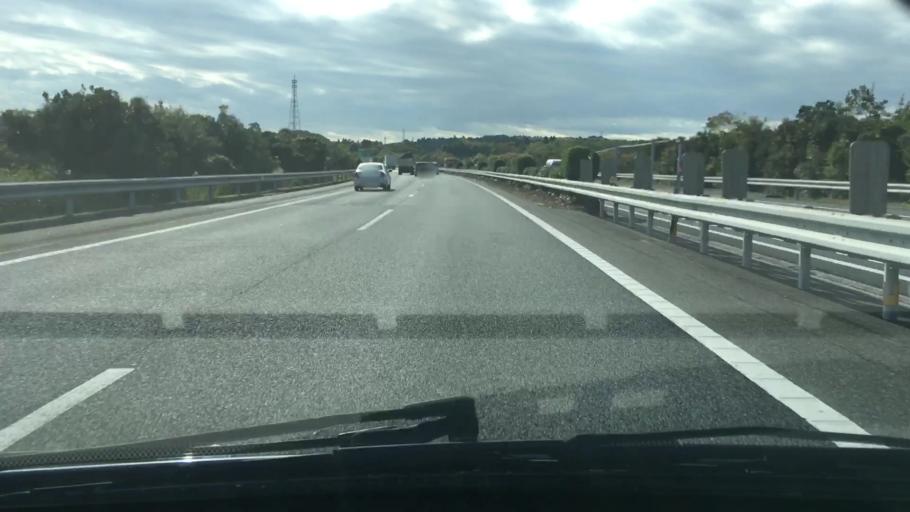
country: JP
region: Chiba
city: Ichihara
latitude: 35.4795
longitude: 140.0811
